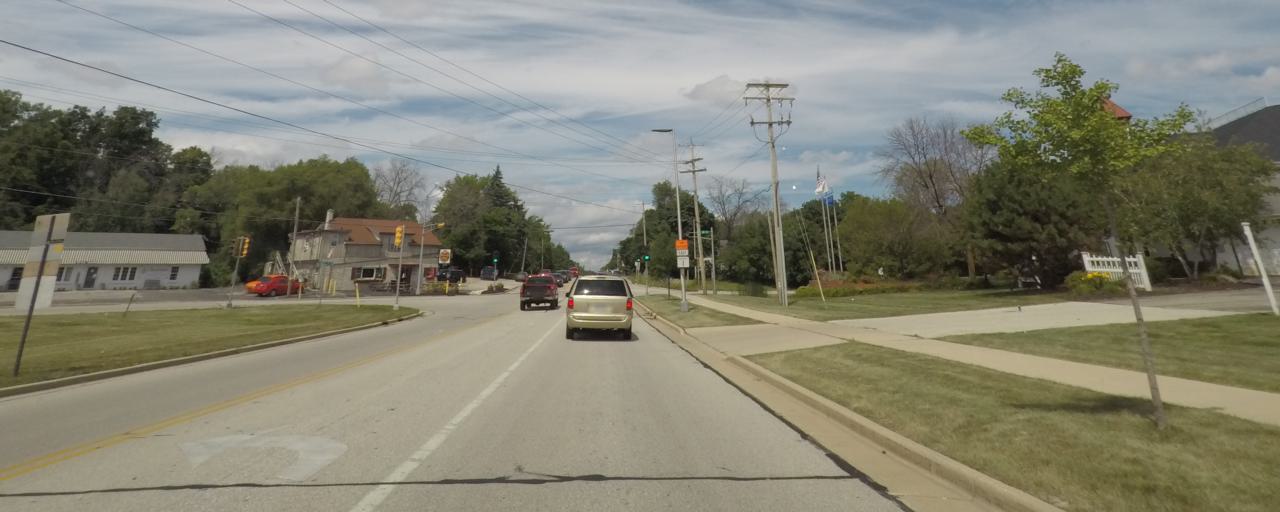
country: US
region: Wisconsin
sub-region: Milwaukee County
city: Hales Corners
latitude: 42.9632
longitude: -88.0691
